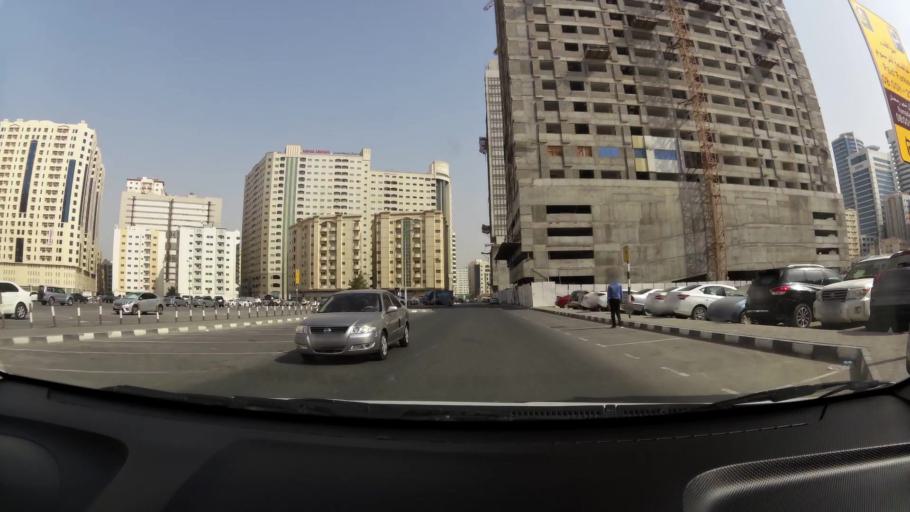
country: AE
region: Ash Shariqah
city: Sharjah
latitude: 25.3417
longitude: 55.3890
